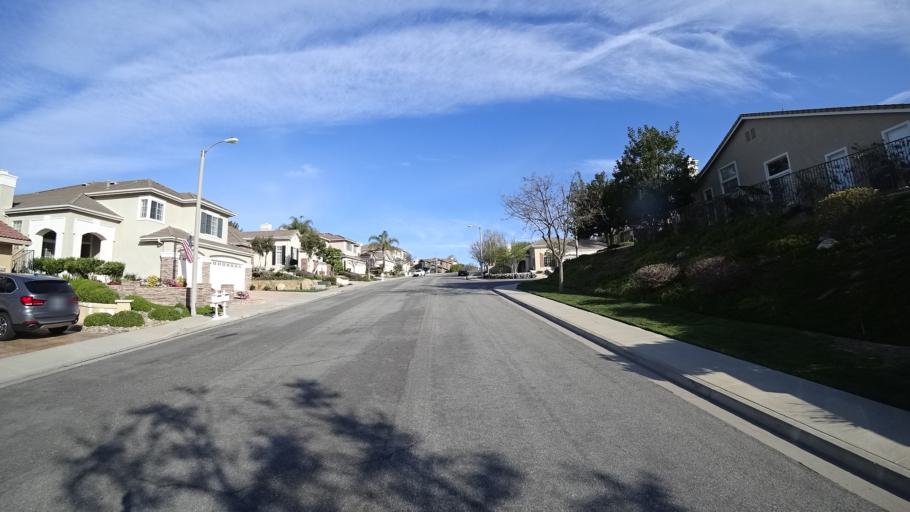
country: US
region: California
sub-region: Ventura County
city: Thousand Oaks
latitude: 34.2147
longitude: -118.8125
